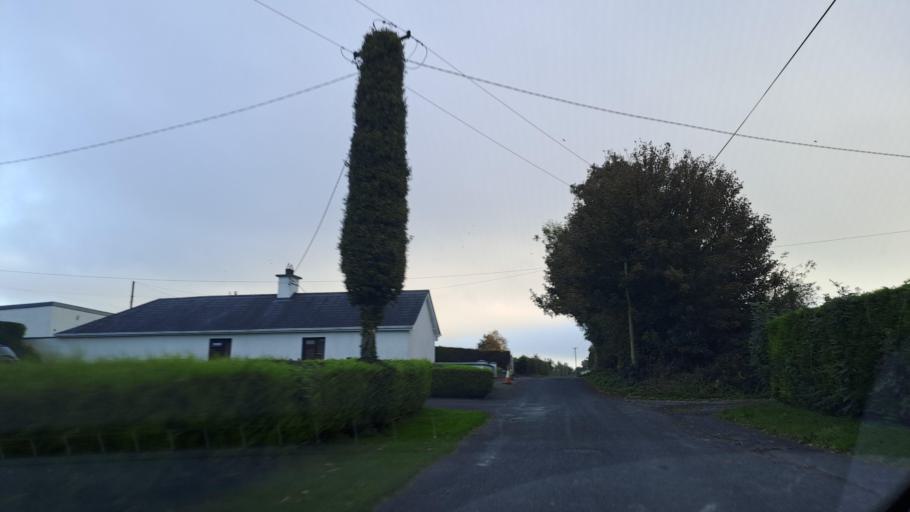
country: IE
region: Ulster
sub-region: County Monaghan
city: Carrickmacross
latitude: 53.9812
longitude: -6.6782
